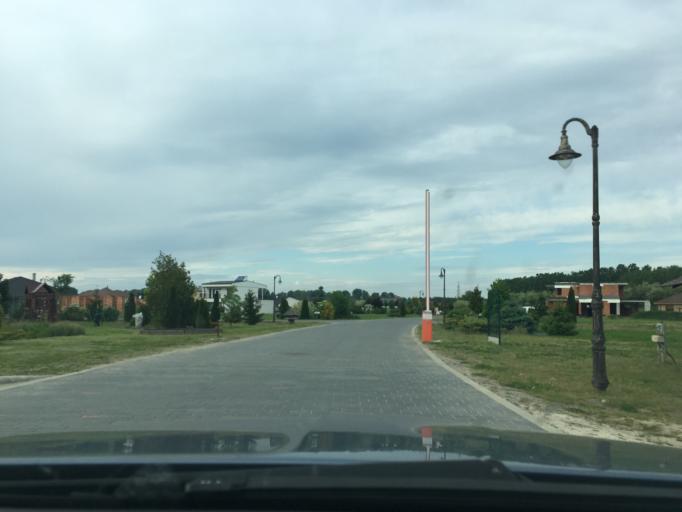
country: HU
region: Hajdu-Bihar
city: Debrecen
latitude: 47.5488
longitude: 21.6884
